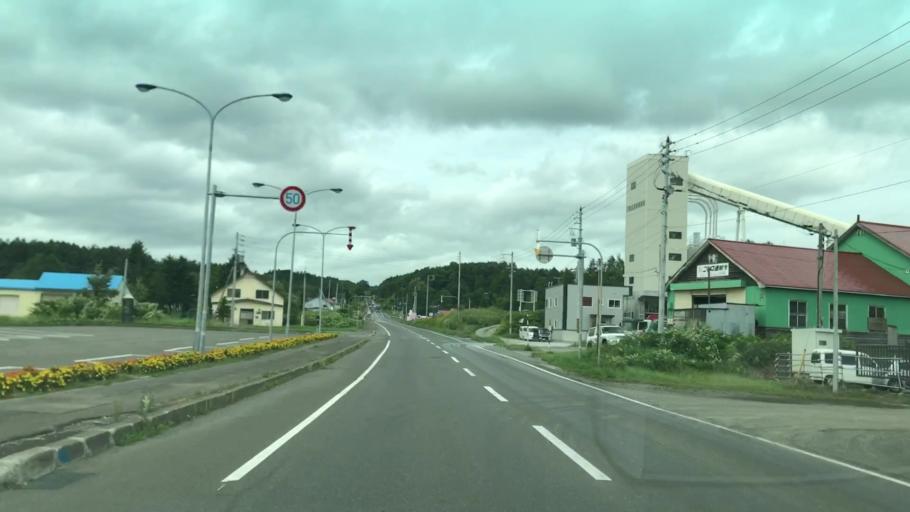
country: JP
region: Hokkaido
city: Niseko Town
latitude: 42.9202
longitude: 140.7423
